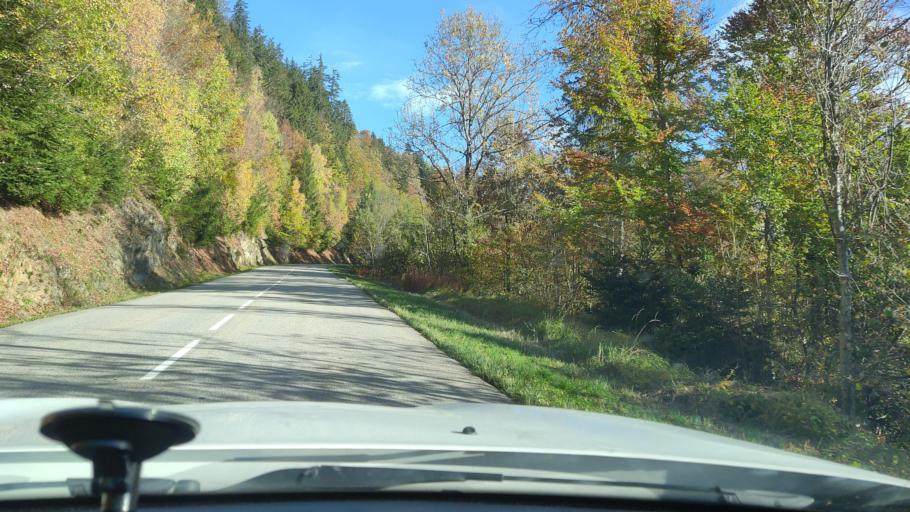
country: FR
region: Rhone-Alpes
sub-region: Departement de la Savoie
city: Beaufort
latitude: 45.7357
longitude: 6.5646
